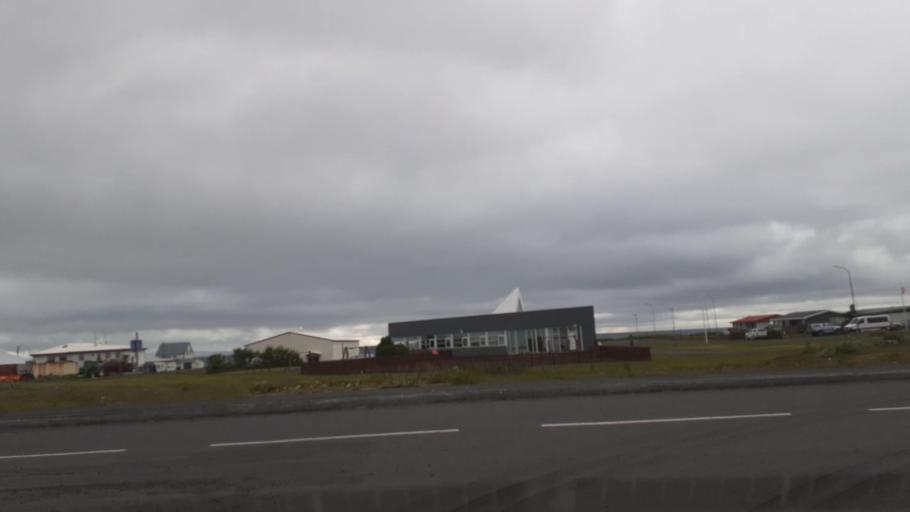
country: IS
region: Northeast
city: Husavik
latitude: 66.3013
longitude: -16.4442
